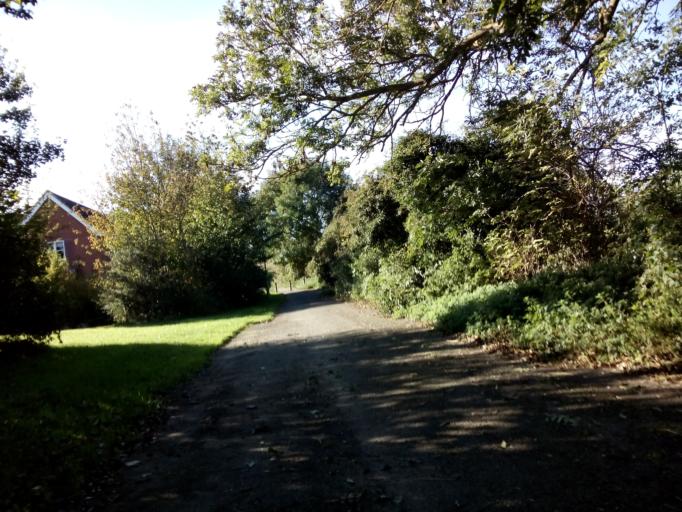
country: GB
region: England
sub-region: Suffolk
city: Bramford
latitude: 52.0343
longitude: 1.1156
